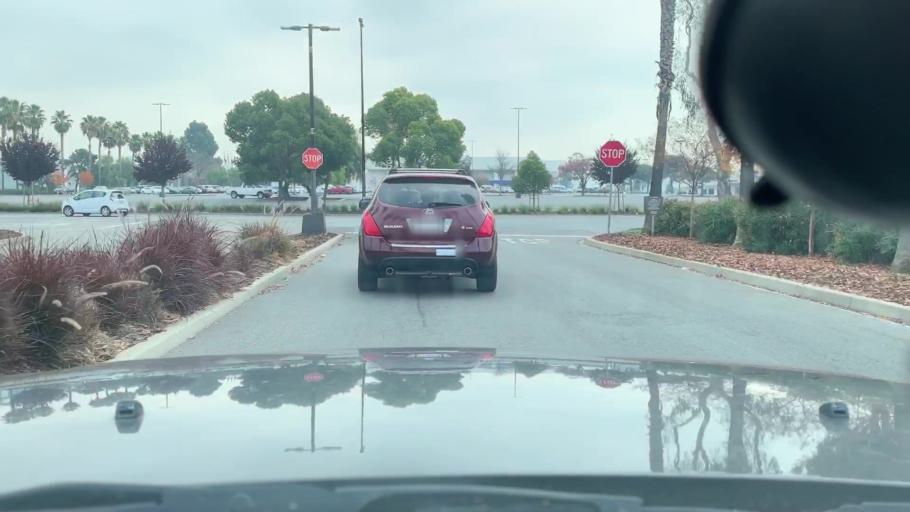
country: US
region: California
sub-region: Santa Clara County
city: Alum Rock
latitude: 37.3270
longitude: -121.8176
